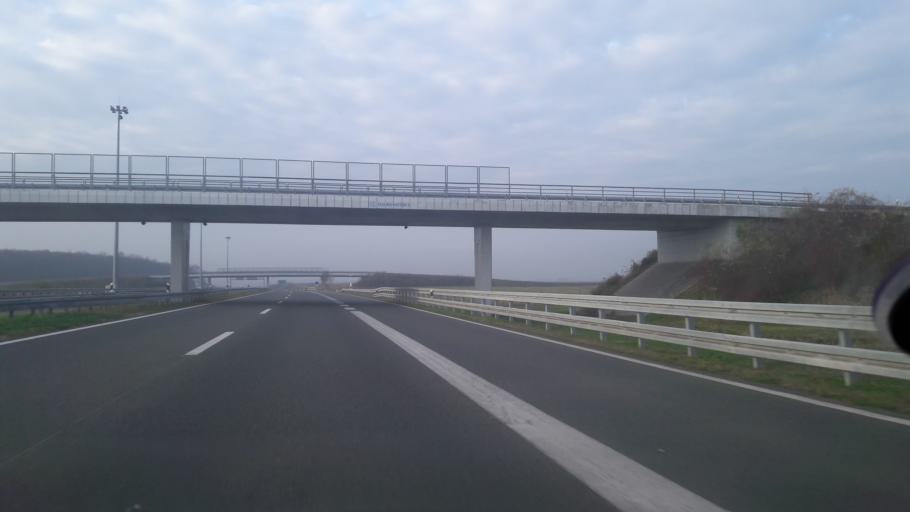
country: HR
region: Osjecko-Baranjska
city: Piskorevci
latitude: 45.3242
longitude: 18.3804
